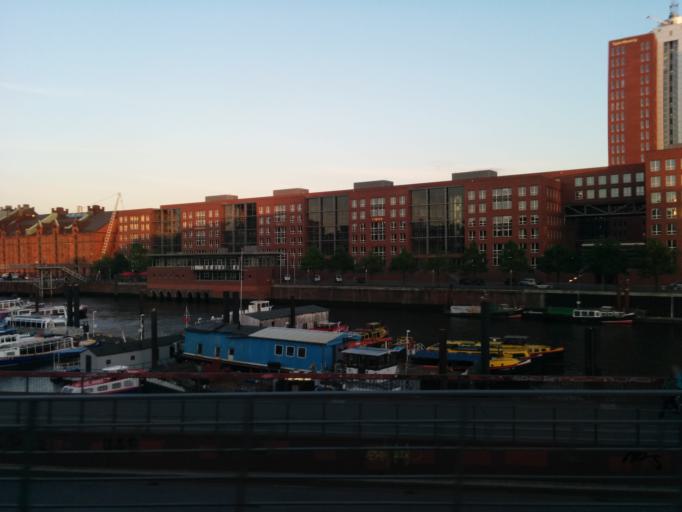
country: DE
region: Hamburg
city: Neustadt
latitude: 53.5449
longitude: 9.9837
